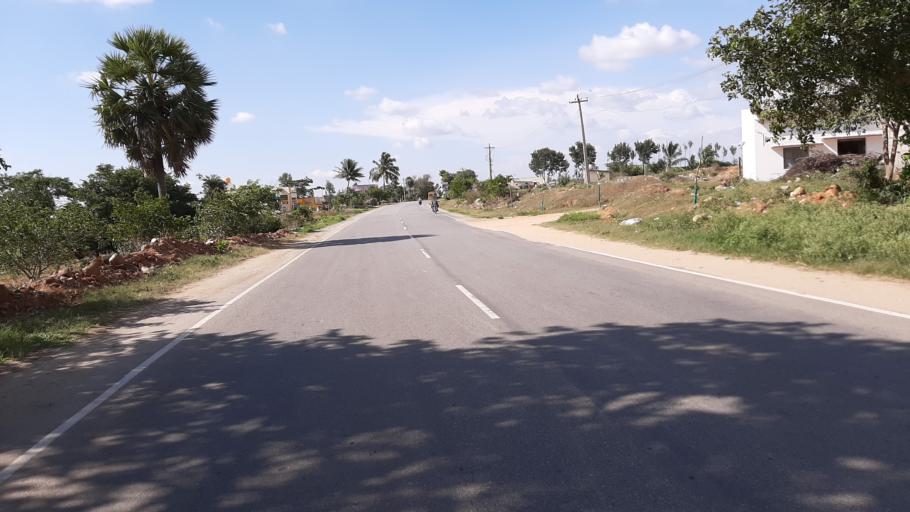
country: IN
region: Tamil Nadu
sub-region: Krishnagiri
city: Denkanikota
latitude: 12.5528
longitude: 77.7856
